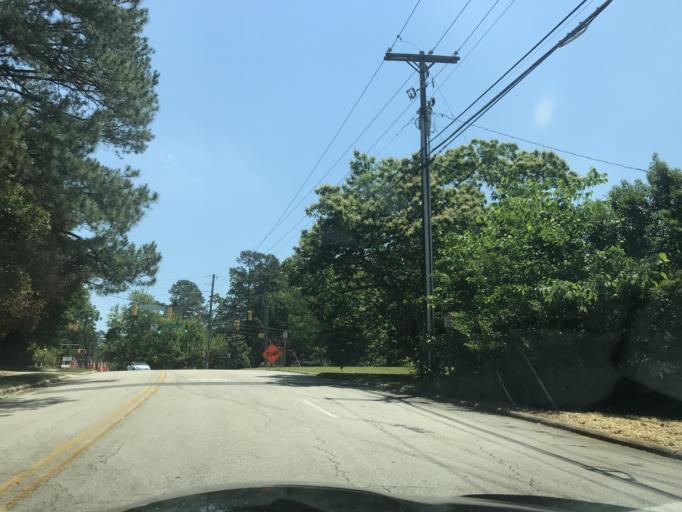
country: US
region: North Carolina
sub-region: Wake County
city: West Raleigh
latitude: 35.8531
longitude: -78.6590
